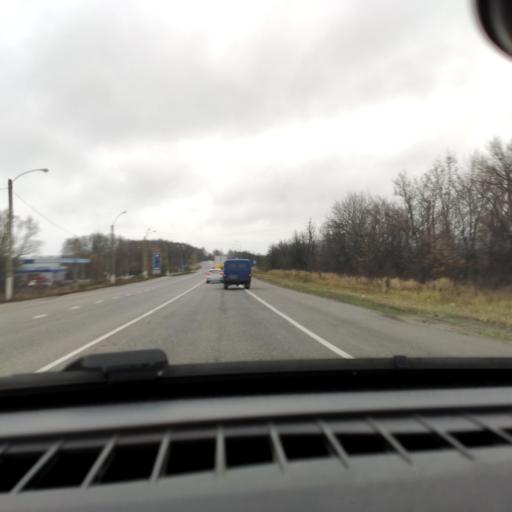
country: RU
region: Voronezj
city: Kolodeznyy
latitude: 51.3321
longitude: 39.0257
